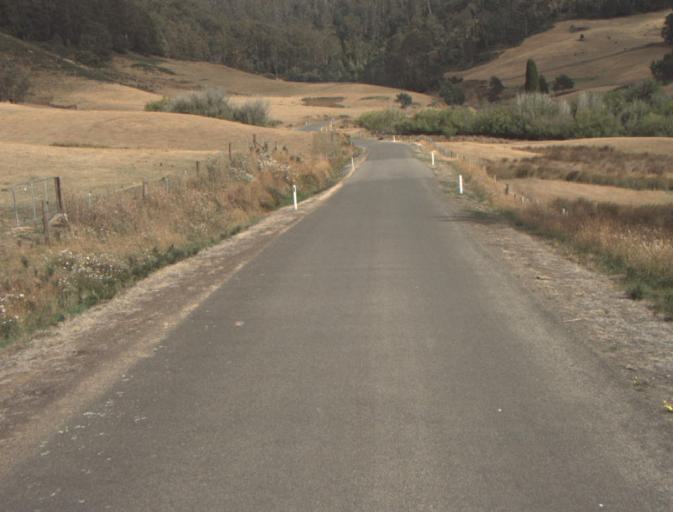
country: AU
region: Tasmania
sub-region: Dorset
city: Scottsdale
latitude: -41.4505
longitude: 147.5902
